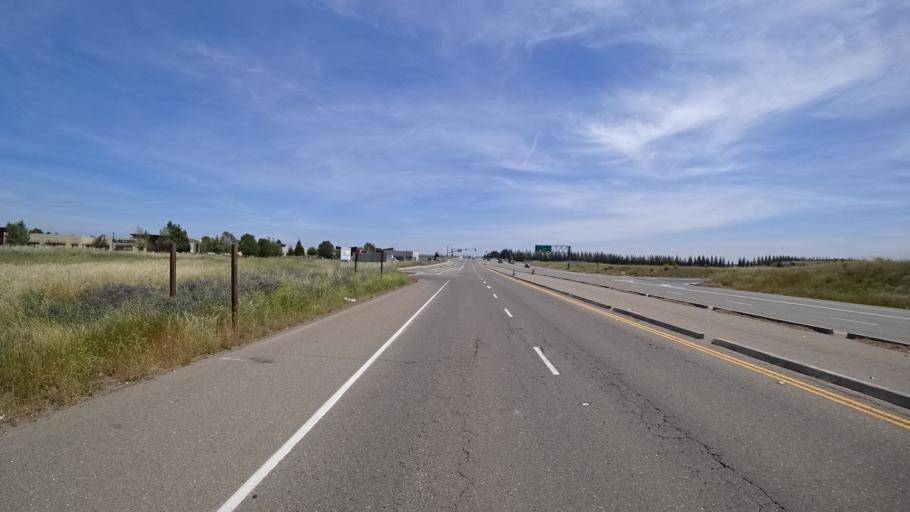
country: US
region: California
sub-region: Placer County
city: Roseville
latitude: 38.8174
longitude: -121.3046
